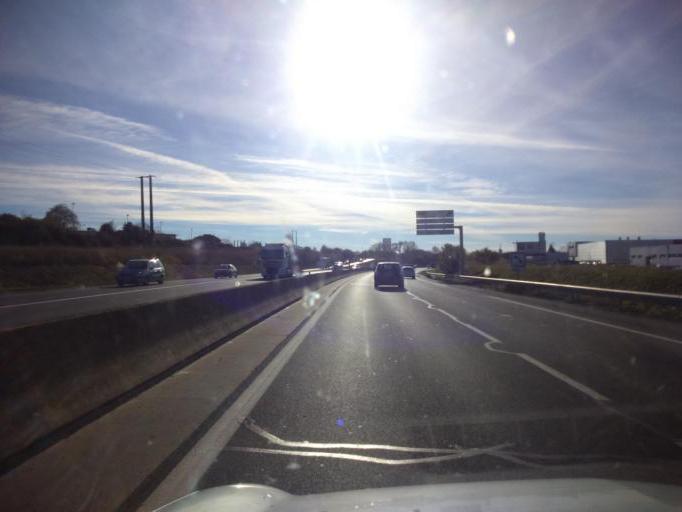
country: FR
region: Poitou-Charentes
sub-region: Departement de la Charente-Maritime
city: Perigny
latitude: 46.1562
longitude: -1.1166
